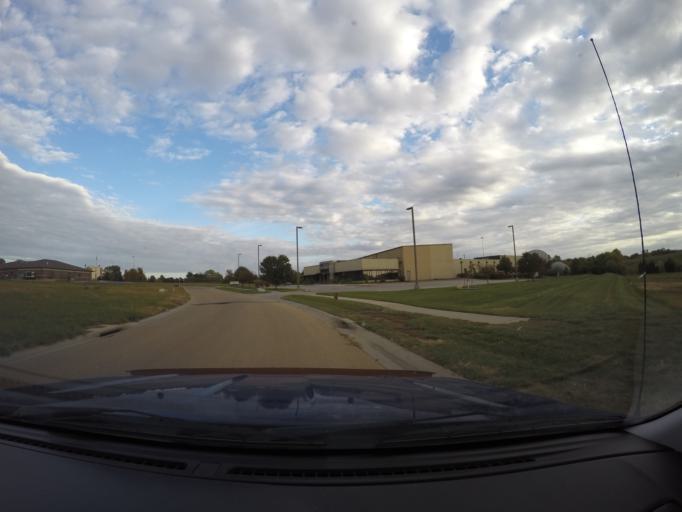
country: US
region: Kansas
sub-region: Shawnee County
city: Topeka
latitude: 39.0558
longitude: -95.7688
